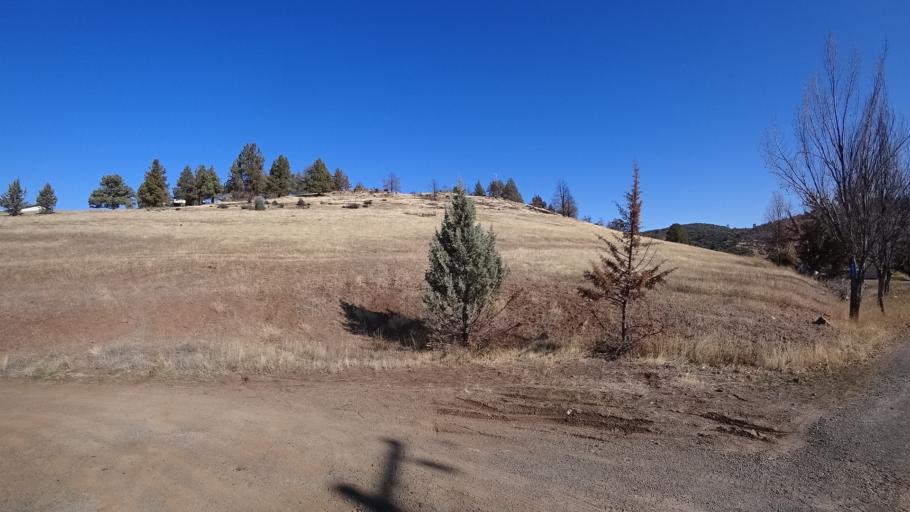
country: US
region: California
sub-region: Siskiyou County
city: Montague
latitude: 41.8974
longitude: -122.4843
